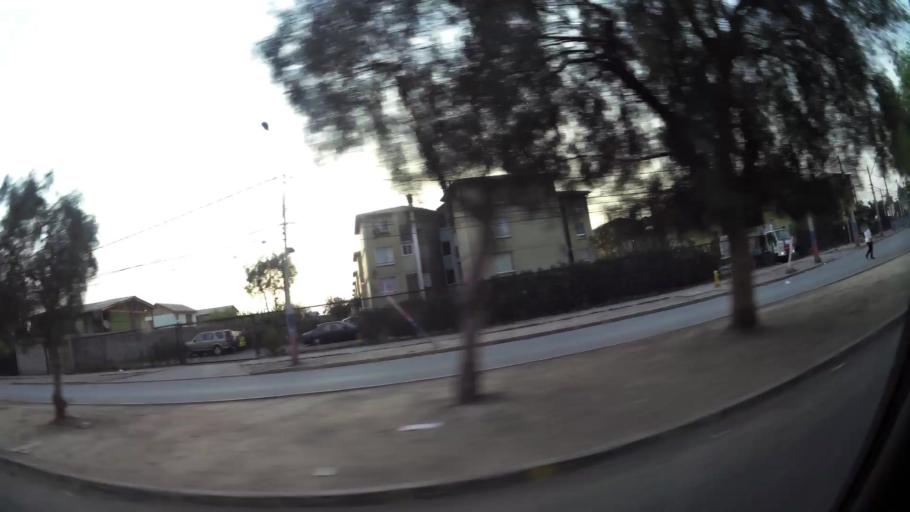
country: CL
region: Santiago Metropolitan
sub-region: Provincia de Santiago
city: Lo Prado
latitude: -33.5078
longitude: -70.7840
